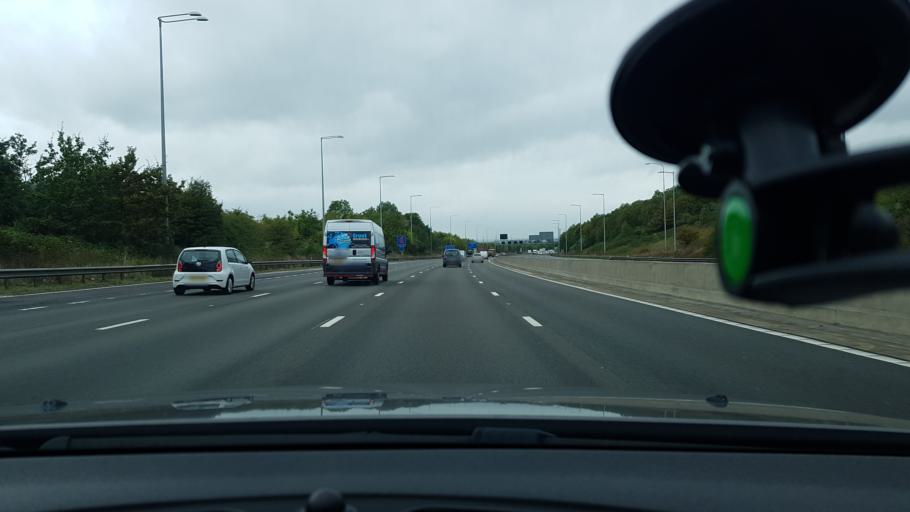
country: GB
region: England
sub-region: Essex
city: Waltham Abbey
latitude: 51.6779
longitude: 0.0279
